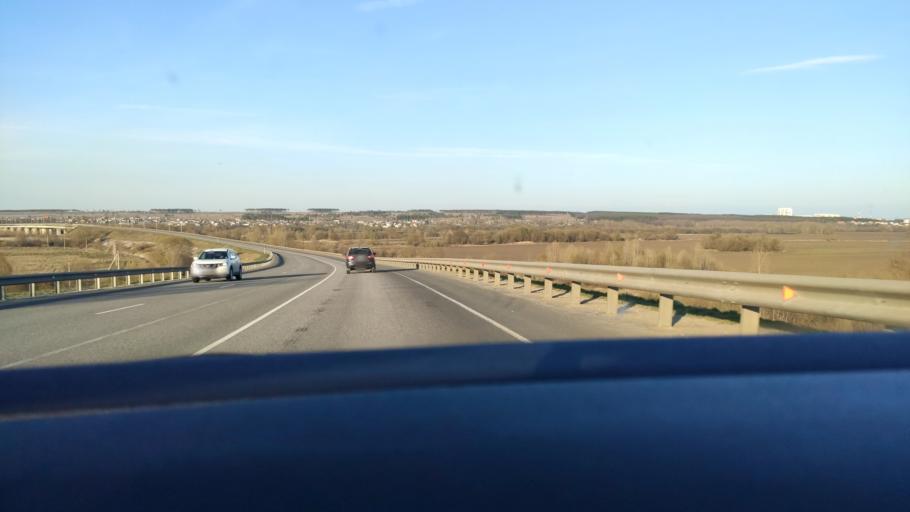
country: RU
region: Voronezj
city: Kolodeznyy
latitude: 51.3296
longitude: 39.1586
